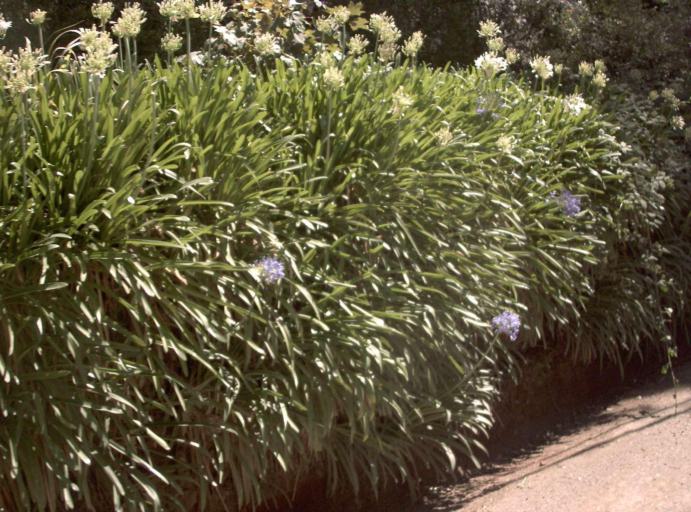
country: AU
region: Victoria
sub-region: Yarra Ranges
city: Mount Dandenong
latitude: -37.8348
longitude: 145.3563
